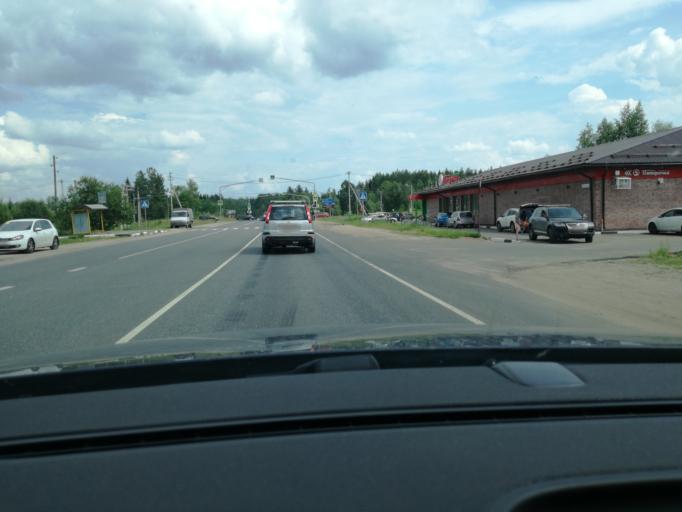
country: RU
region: Moskovskaya
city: Khot'kovo
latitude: 56.3107
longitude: 37.9350
